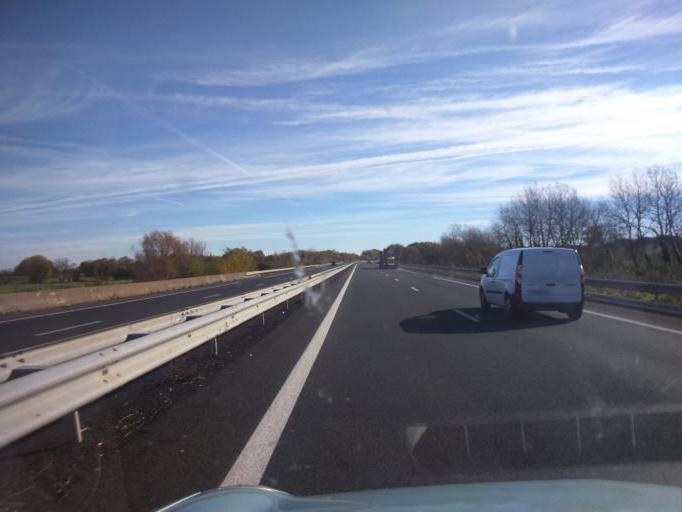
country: FR
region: Poitou-Charentes
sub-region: Departement de la Charente-Maritime
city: Tonnay-Charente
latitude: 45.9574
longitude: -0.9223
